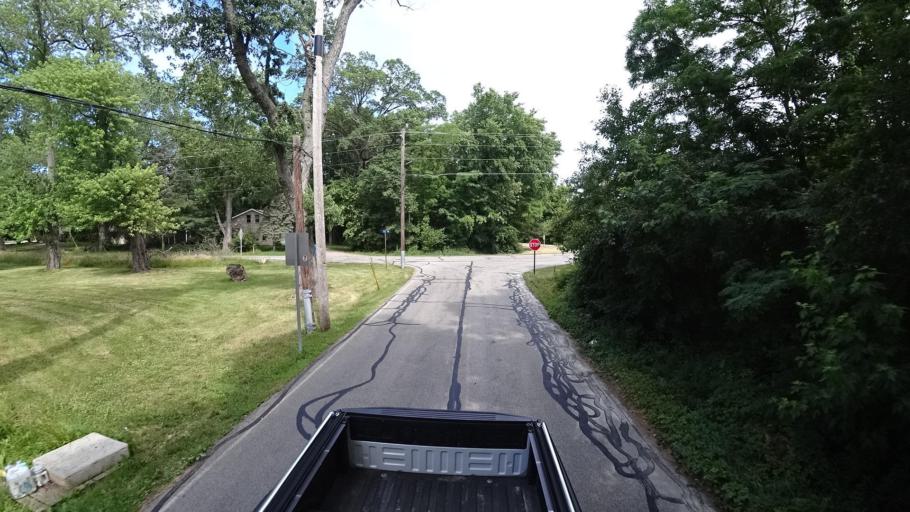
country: US
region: Indiana
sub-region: Porter County
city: Porter
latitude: 41.6074
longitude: -87.0820
